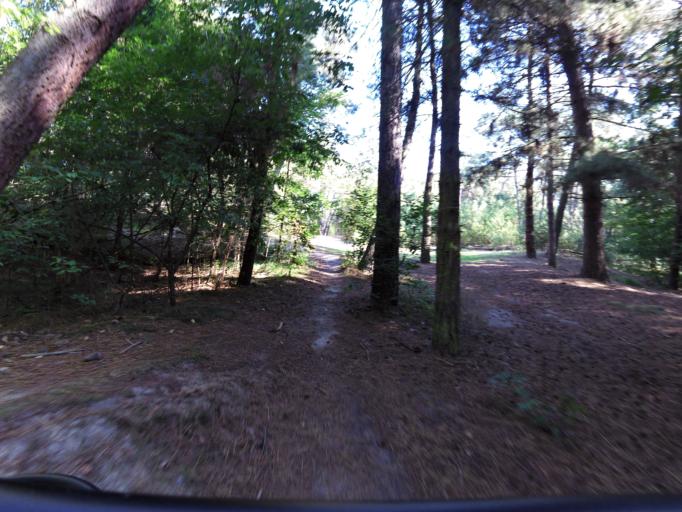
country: BE
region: Flanders
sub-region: Provincie Antwerpen
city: Stabroek
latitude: 51.3592
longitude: 4.3475
